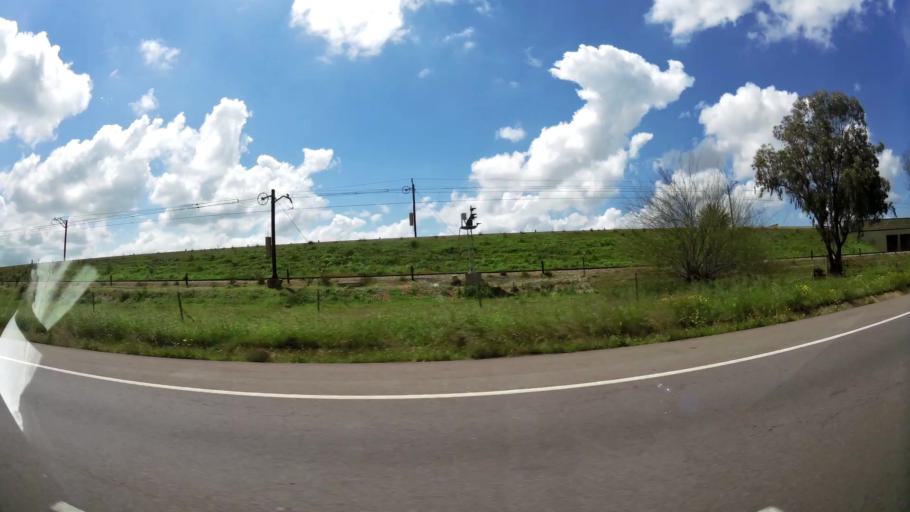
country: MA
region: Chaouia-Ouardigha
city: Nouaseur
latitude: 33.4084
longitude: -7.6256
